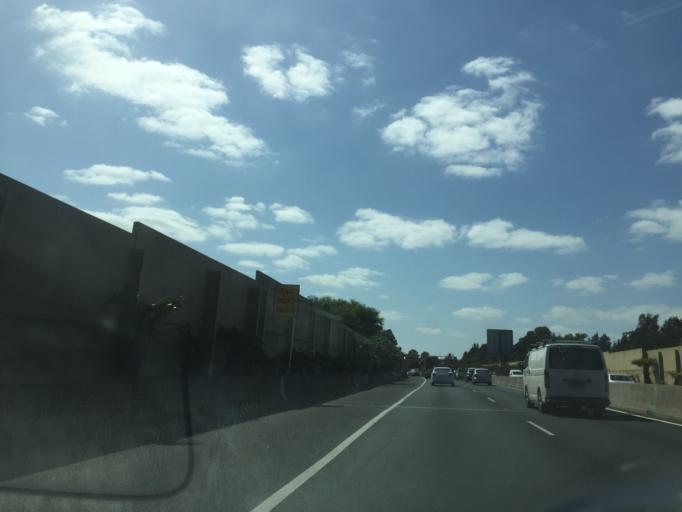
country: AU
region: New South Wales
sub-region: Canterbury
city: Clemton Park
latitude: -33.9402
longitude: 151.0884
